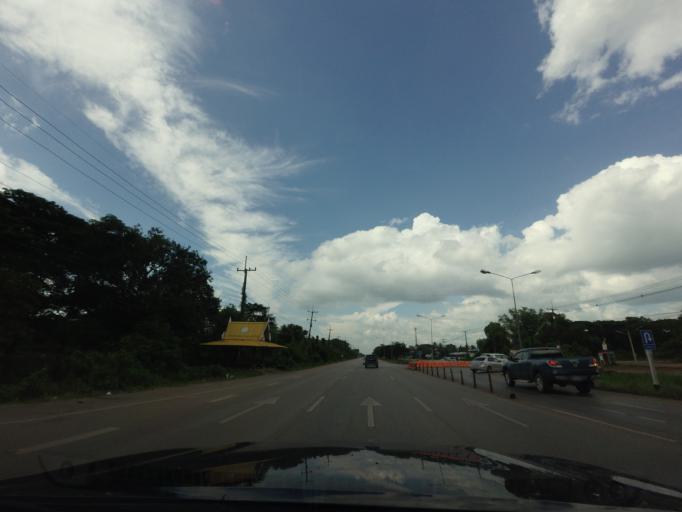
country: TH
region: Changwat Udon Thani
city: Udon Thani
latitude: 17.5364
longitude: 102.8000
